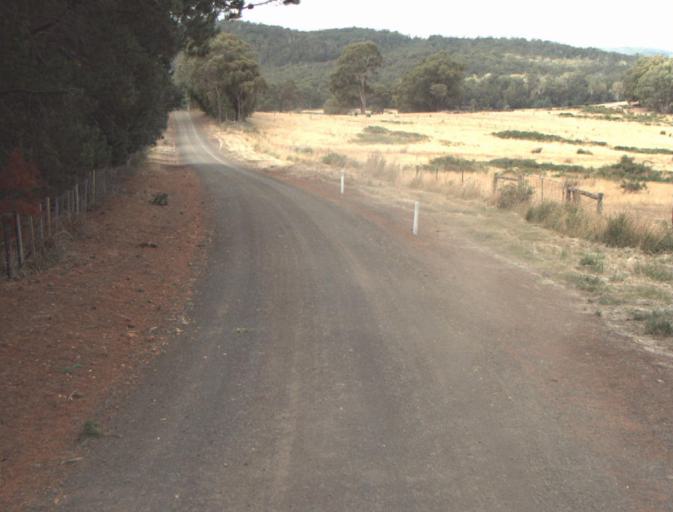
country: AU
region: Tasmania
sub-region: Launceston
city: Mayfield
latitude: -41.2813
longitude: 147.0423
